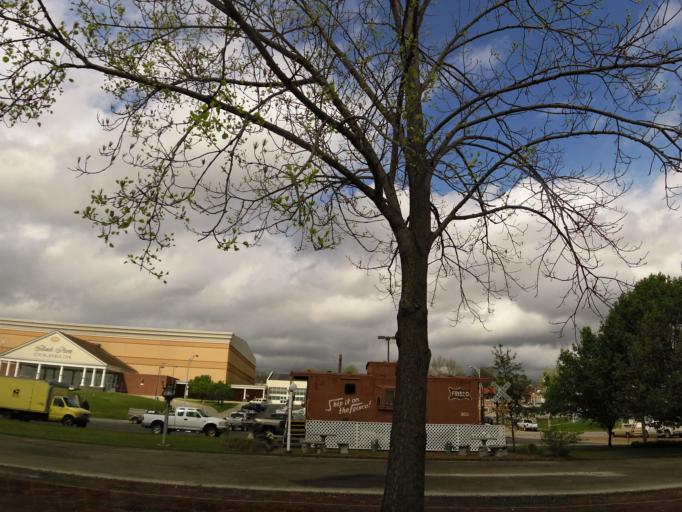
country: US
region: Missouri
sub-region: Butler County
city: Poplar Bluff
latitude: 36.7548
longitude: -90.3952
